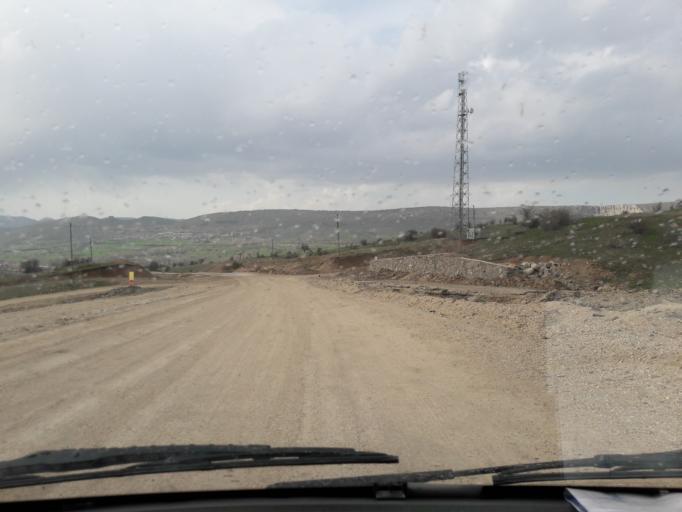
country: TR
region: Giresun
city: Alucra
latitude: 40.3194
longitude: 38.7738
